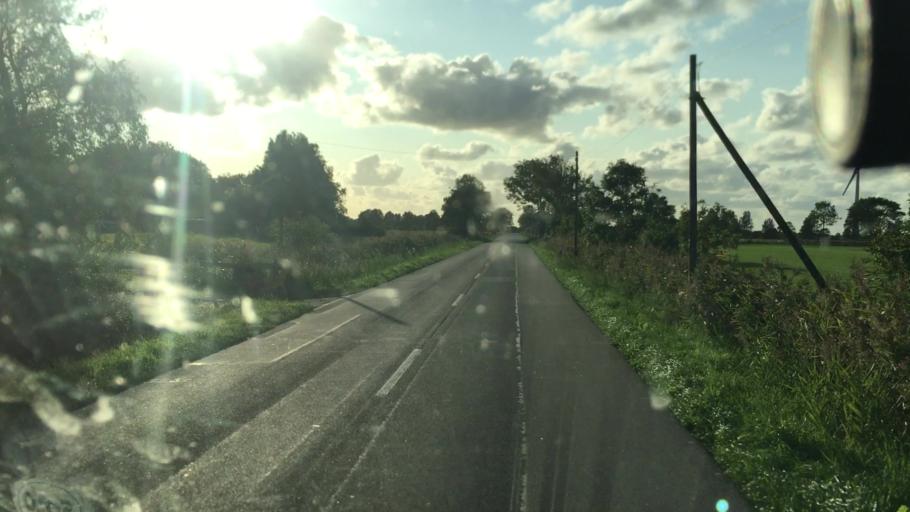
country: DE
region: Lower Saxony
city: Werdum
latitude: 53.6615
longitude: 7.7619
